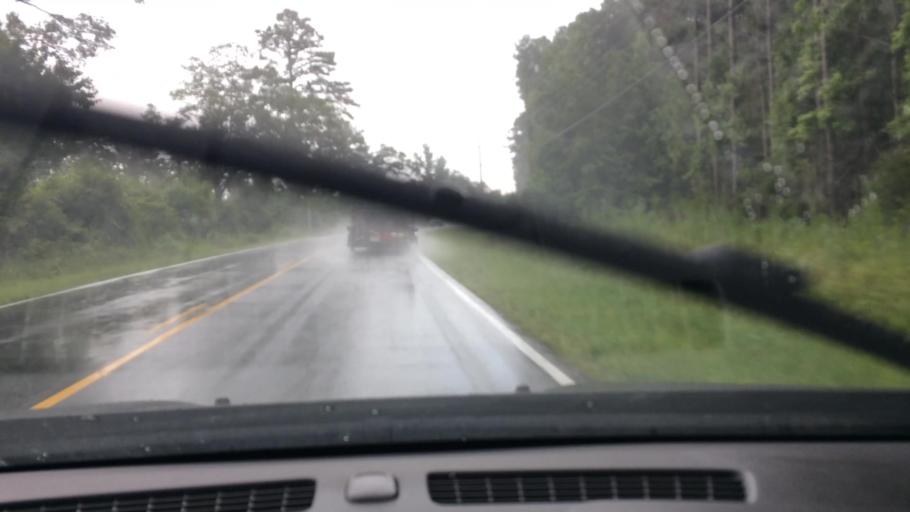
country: US
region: North Carolina
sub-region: Pitt County
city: Winterville
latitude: 35.5134
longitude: -77.3822
